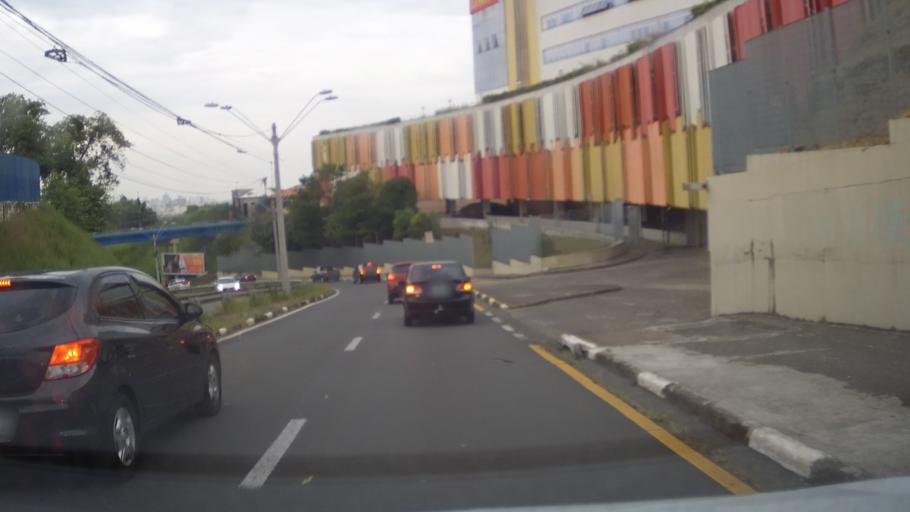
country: BR
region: Sao Paulo
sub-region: Campinas
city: Campinas
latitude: -22.9257
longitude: -47.0381
